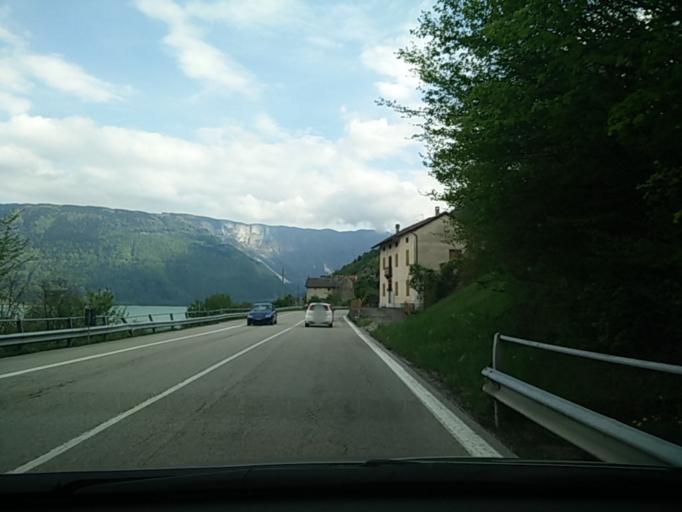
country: IT
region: Veneto
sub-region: Provincia di Belluno
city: Farra d'Alpago
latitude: 46.1276
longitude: 12.3183
